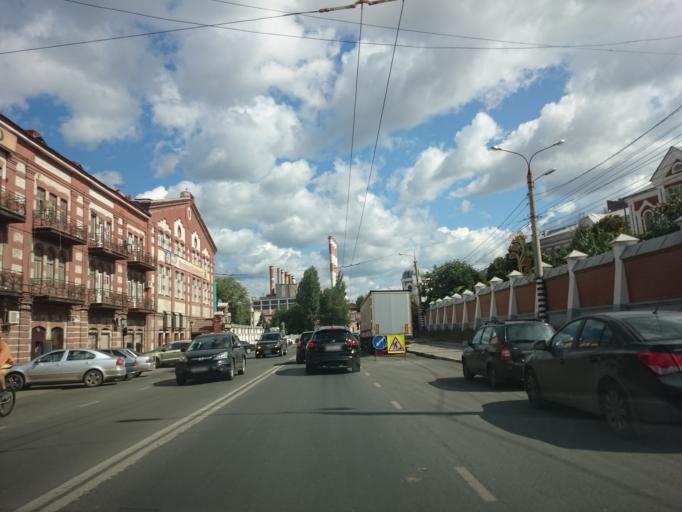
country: RU
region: Samara
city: Samara
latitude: 53.2003
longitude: 50.0986
